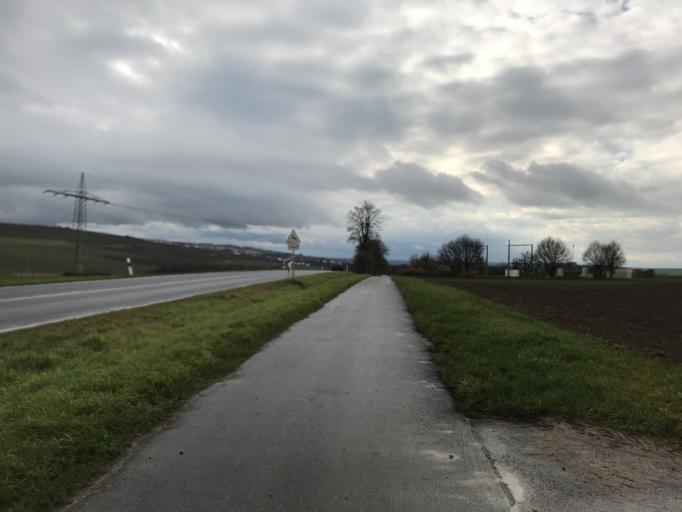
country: DE
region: Rheinland-Pfalz
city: Klein-Winternheim
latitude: 49.9294
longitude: 8.2074
